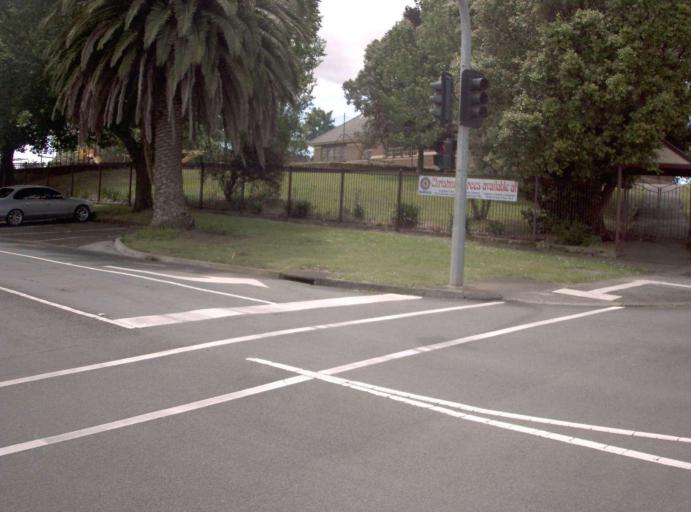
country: AU
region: Victoria
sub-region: Baw Baw
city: Warragul
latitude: -38.1589
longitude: 145.9300
